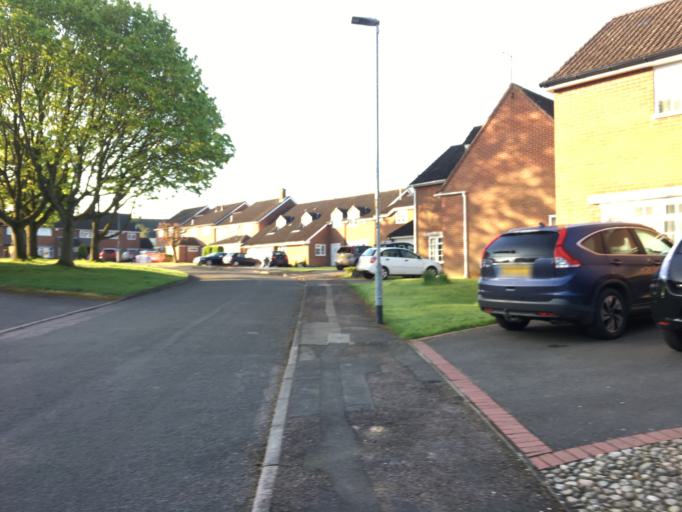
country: GB
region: England
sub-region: Leicestershire
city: Houghton on the Hill
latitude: 52.6256
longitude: -1.0008
